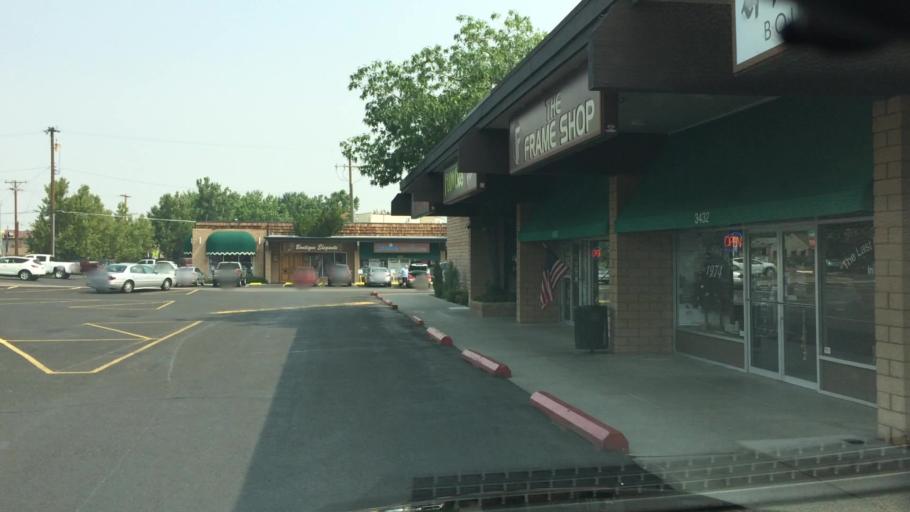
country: US
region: Nevada
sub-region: Washoe County
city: Reno
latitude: 39.4924
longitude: -119.8075
